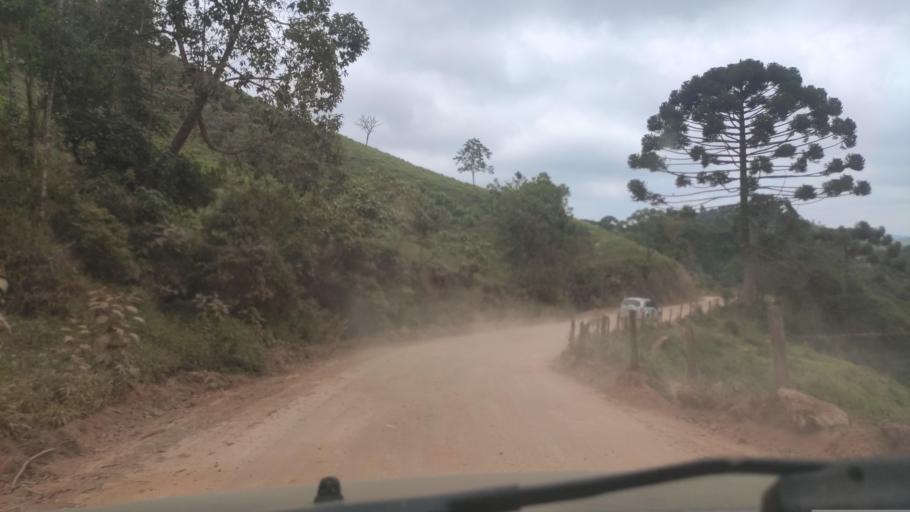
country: BR
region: Minas Gerais
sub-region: Paraisopolis
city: Paraisopolis
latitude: -22.6604
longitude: -45.8833
